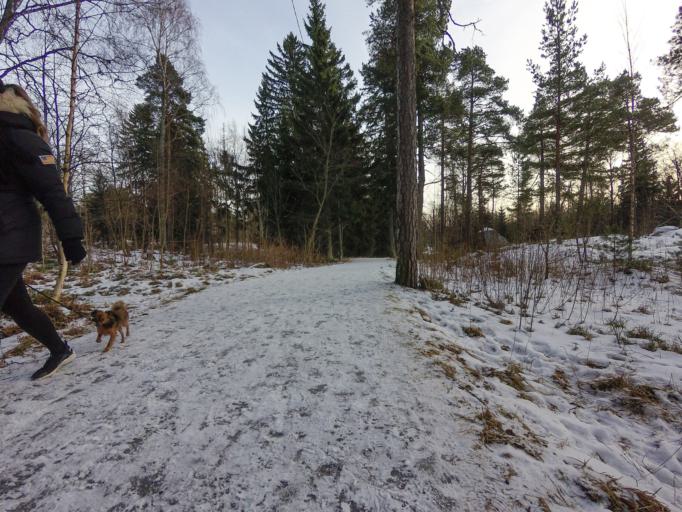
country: FI
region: Uusimaa
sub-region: Helsinki
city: Helsinki
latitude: 60.1657
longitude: 25.0370
